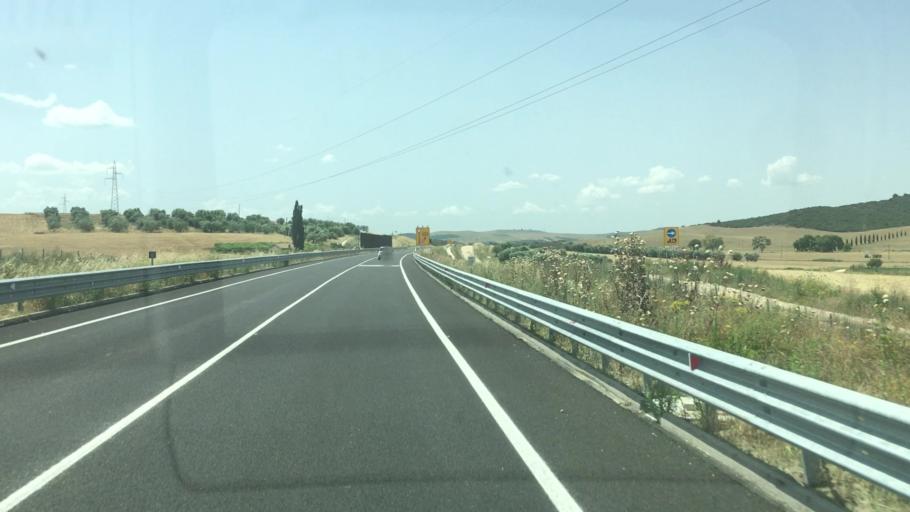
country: IT
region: Basilicate
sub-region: Provincia di Matera
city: La Martella
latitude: 40.6714
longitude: 16.5003
